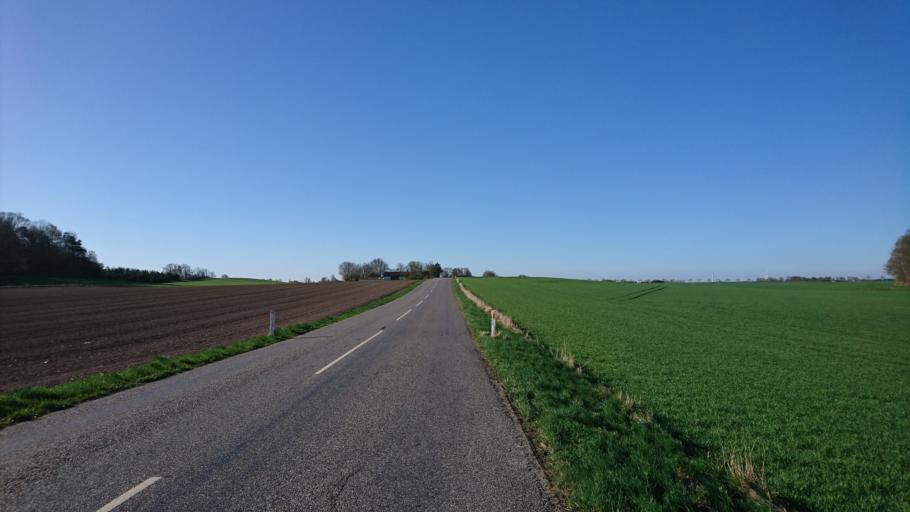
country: DK
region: Capital Region
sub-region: Frederikssund Kommune
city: Skibby
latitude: 55.7358
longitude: 11.9290
